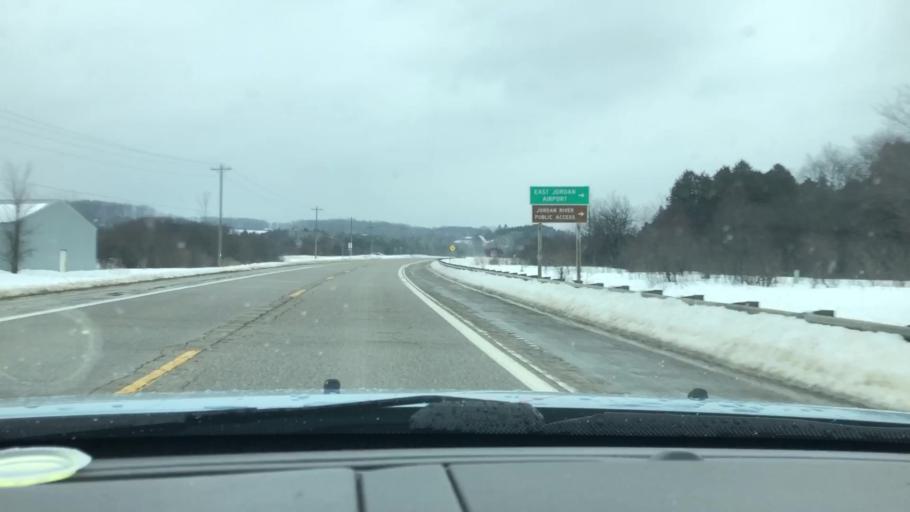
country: US
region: Michigan
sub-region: Charlevoix County
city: East Jordan
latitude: 45.1306
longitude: -85.1385
